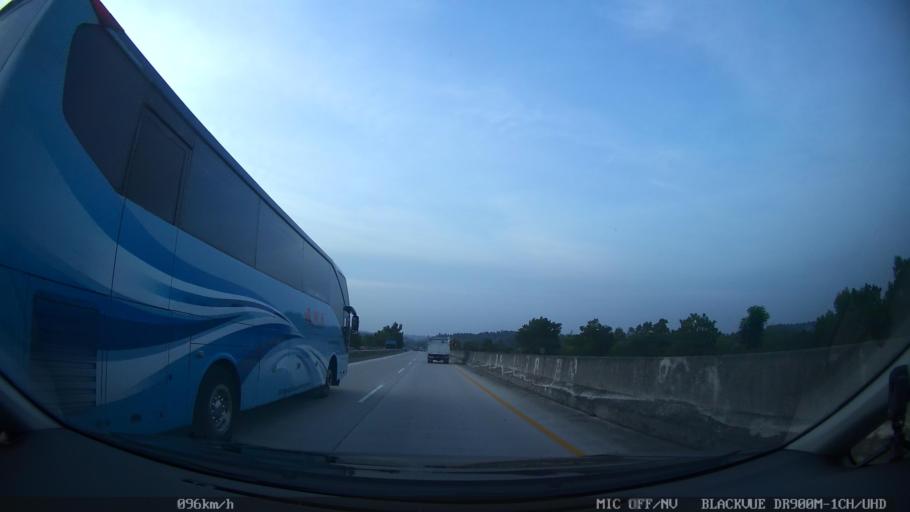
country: ID
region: Lampung
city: Penengahan
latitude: -5.7858
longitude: 105.7237
